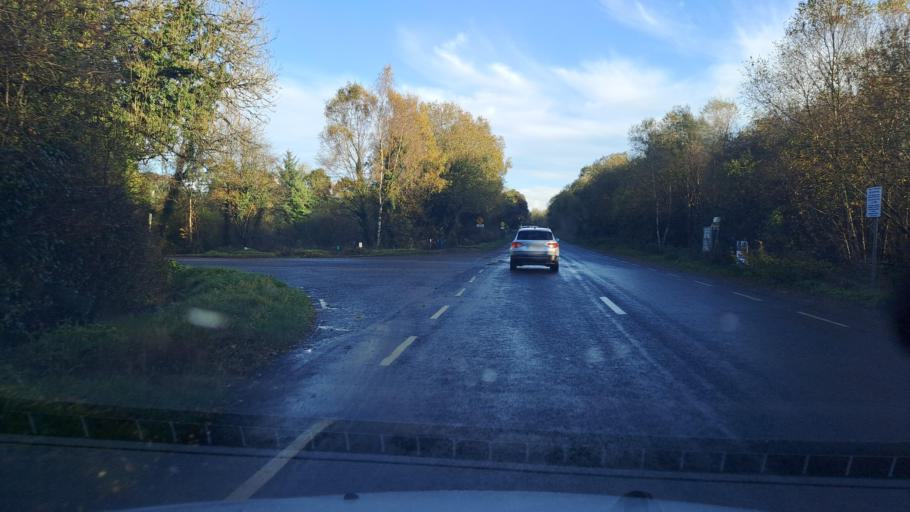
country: IE
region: Ulster
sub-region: An Cabhan
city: Cootehill
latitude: 54.0946
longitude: -7.0842
